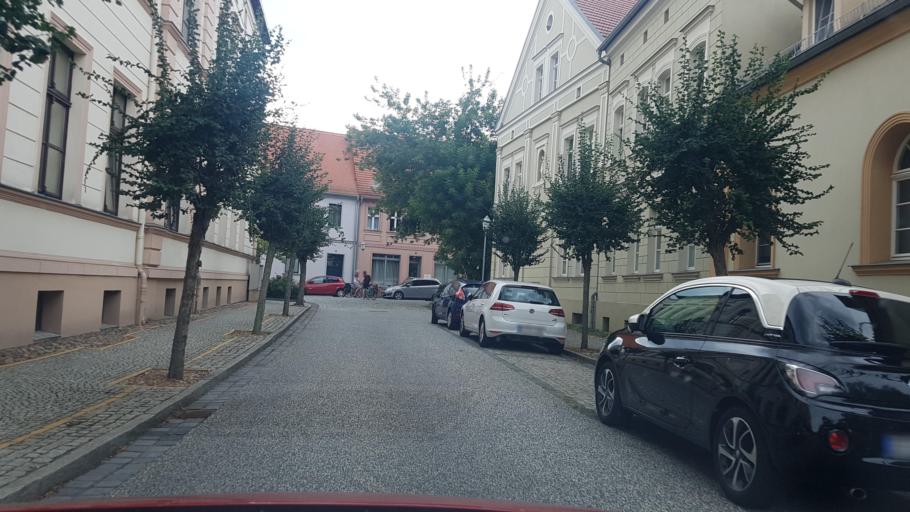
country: DE
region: Brandenburg
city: Herzberg
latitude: 51.6935
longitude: 13.2376
